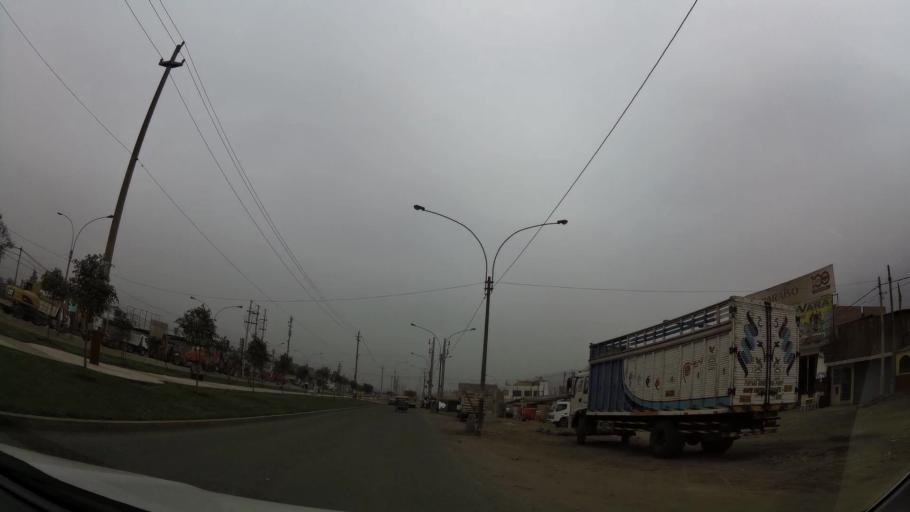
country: PE
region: Lima
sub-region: Lima
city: Urb. Santo Domingo
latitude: -11.9249
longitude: -76.9633
